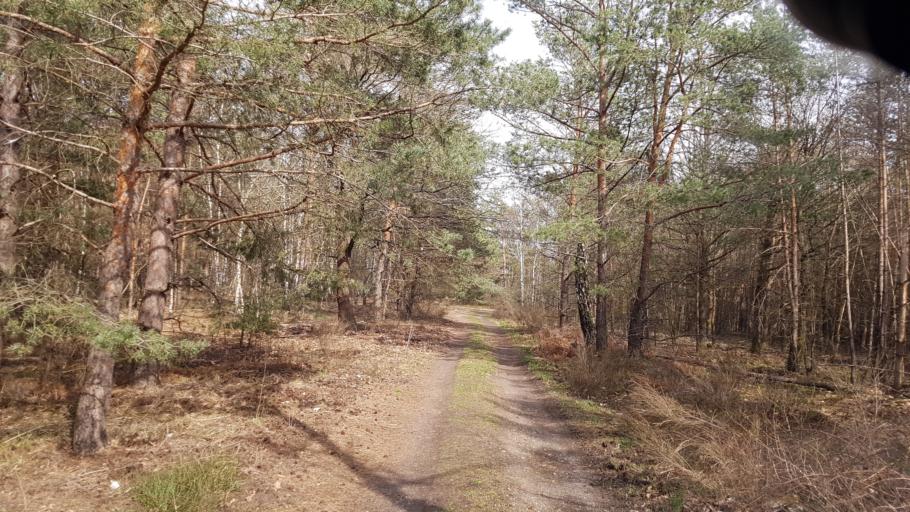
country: DE
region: Brandenburg
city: Lauchhammer
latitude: 51.5398
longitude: 13.7144
